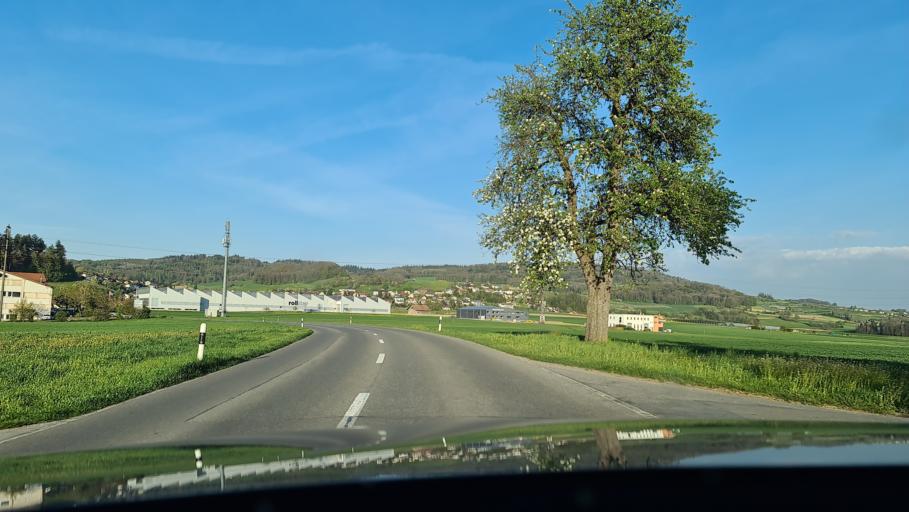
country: CH
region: Aargau
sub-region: Bezirk Lenzburg
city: Seon
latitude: 47.3472
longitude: 8.1710
